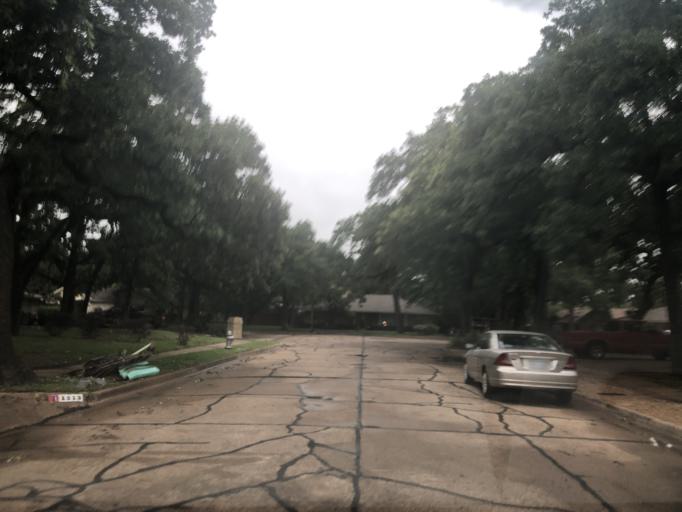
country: US
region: Texas
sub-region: Dallas County
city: Irving
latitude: 32.7986
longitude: -96.9482
